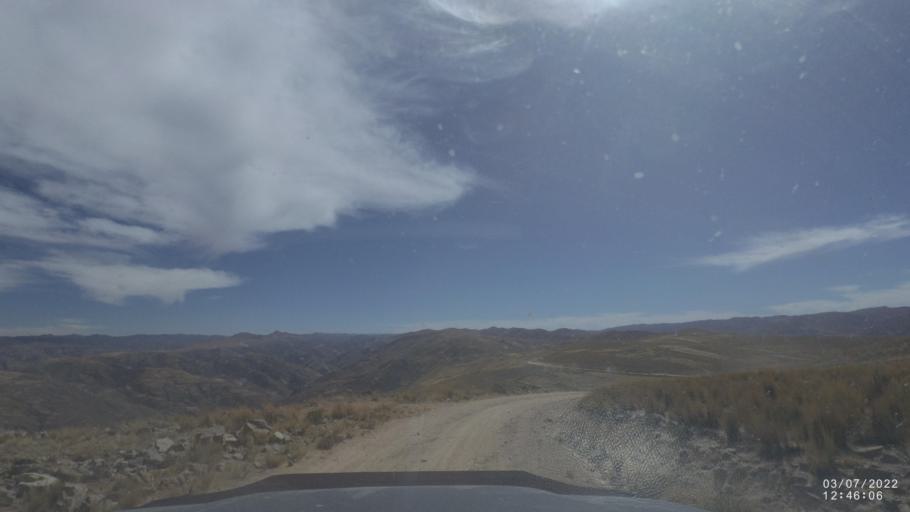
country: BO
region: Cochabamba
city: Irpa Irpa
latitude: -17.7747
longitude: -66.6382
